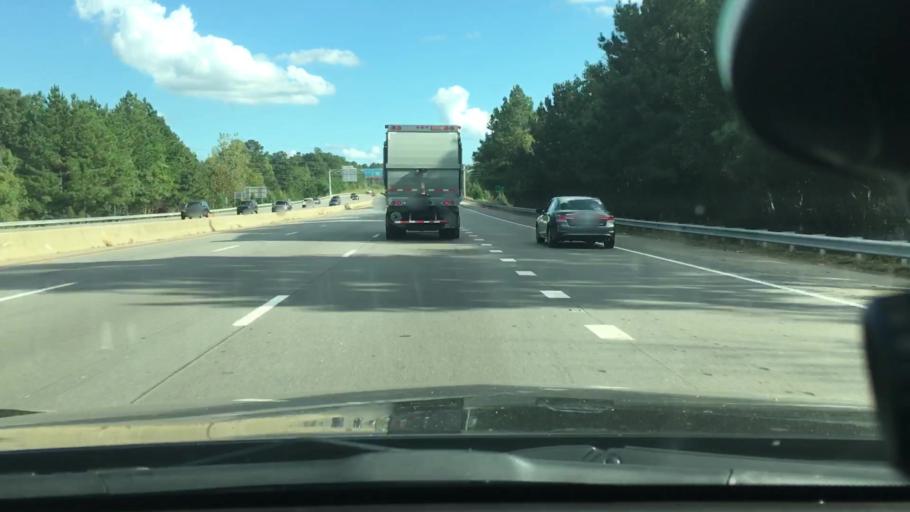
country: US
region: North Carolina
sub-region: Wake County
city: Raleigh
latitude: 35.7920
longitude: -78.5793
